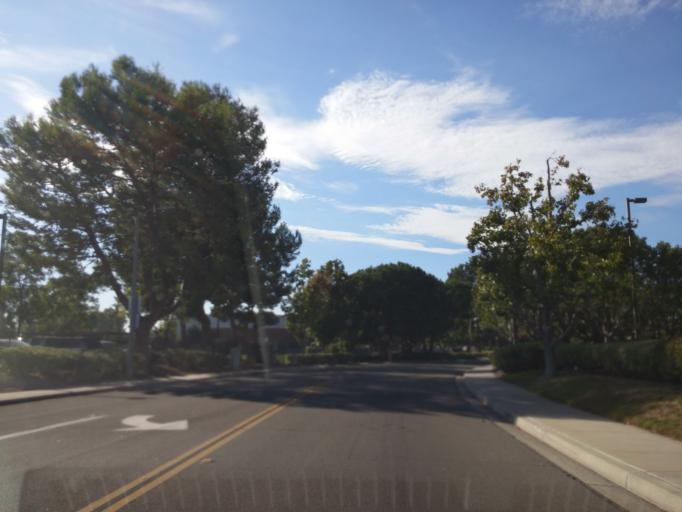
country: US
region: California
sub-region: Orange County
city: Irvine
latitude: 33.6746
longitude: -117.7897
